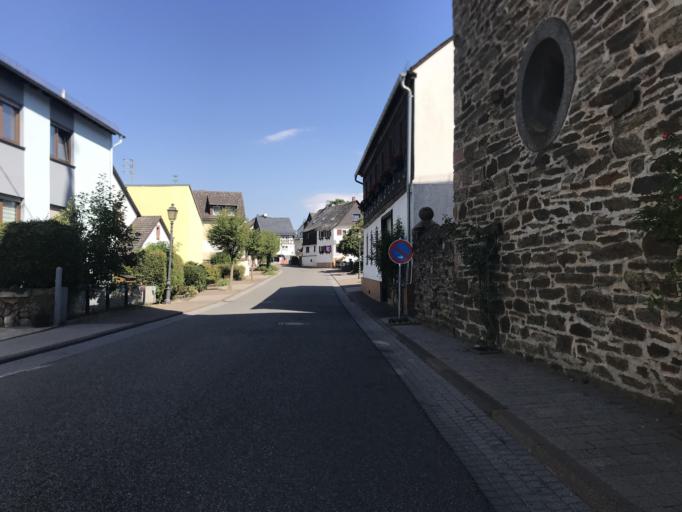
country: DE
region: Rheinland-Pfalz
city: Trechtingshausen
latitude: 50.0521
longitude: 7.8929
